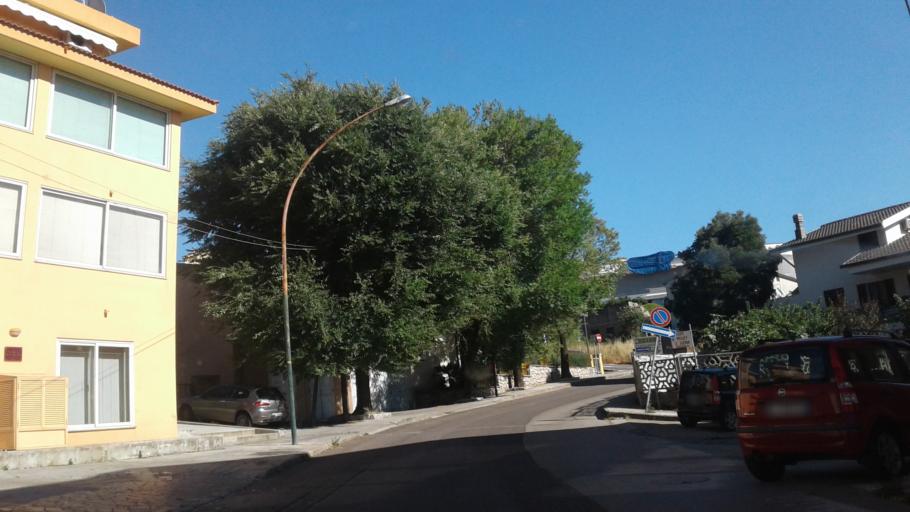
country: IT
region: Sardinia
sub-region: Provincia di Olbia-Tempio
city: Tempio Pausania
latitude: 40.9035
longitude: 9.0999
